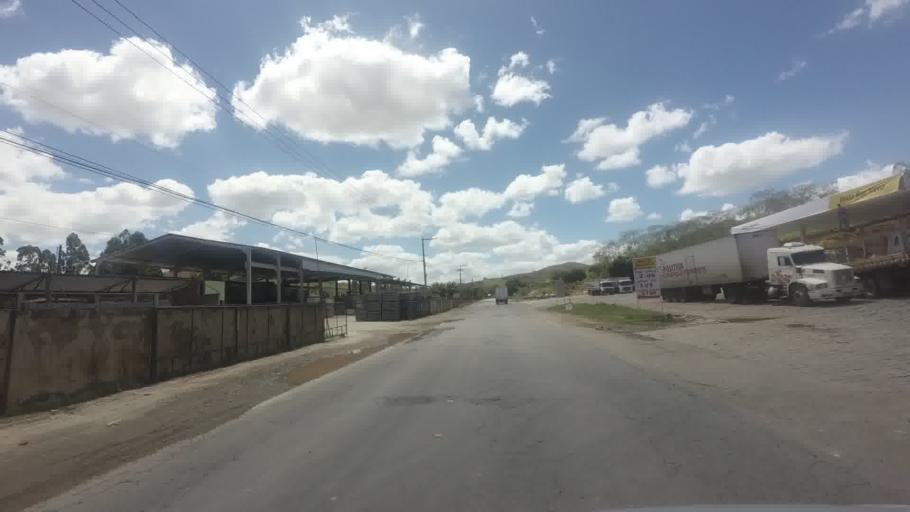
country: BR
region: Rio de Janeiro
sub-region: Santo Antonio De Padua
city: Santo Antonio de Padua
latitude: -21.6388
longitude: -42.2761
